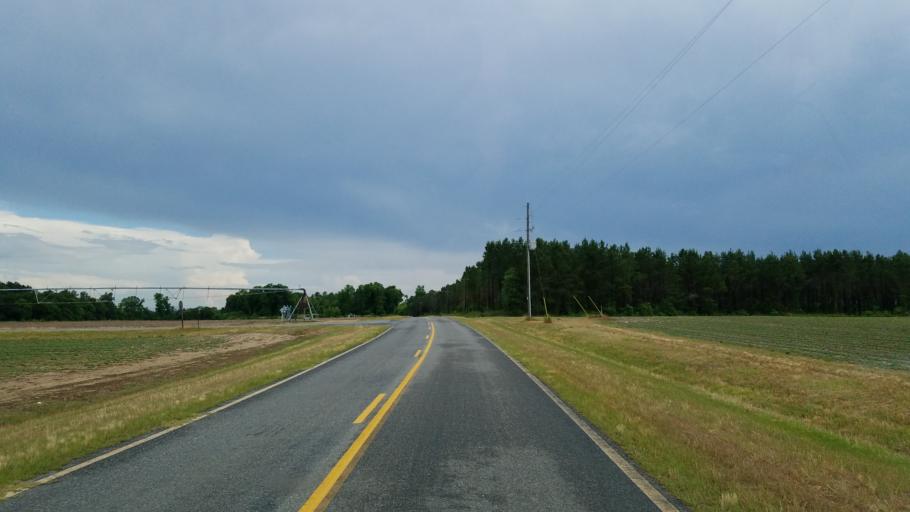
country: US
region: Georgia
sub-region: Dooly County
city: Unadilla
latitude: 32.2086
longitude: -83.7979
